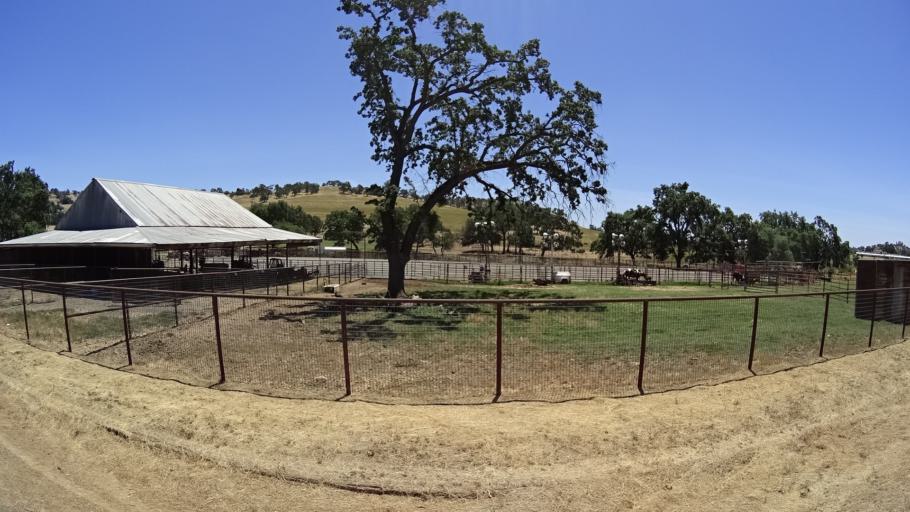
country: US
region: California
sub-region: Calaveras County
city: Valley Springs
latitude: 38.2342
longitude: -120.8111
